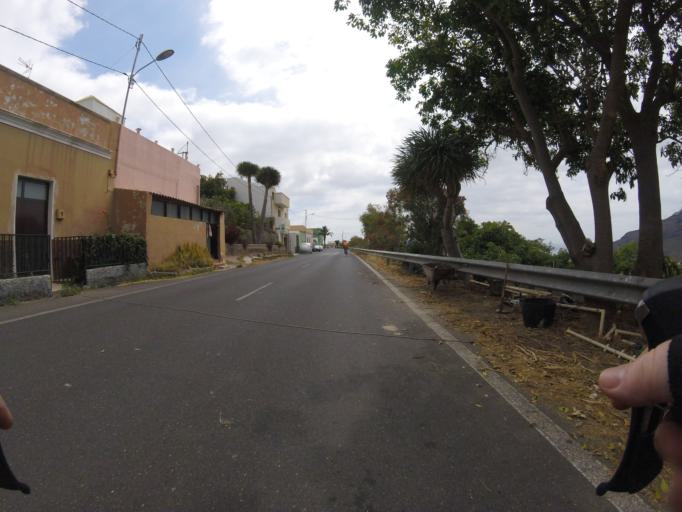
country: ES
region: Canary Islands
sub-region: Provincia de Santa Cruz de Tenerife
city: Guimar
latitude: 28.3083
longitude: -16.4136
